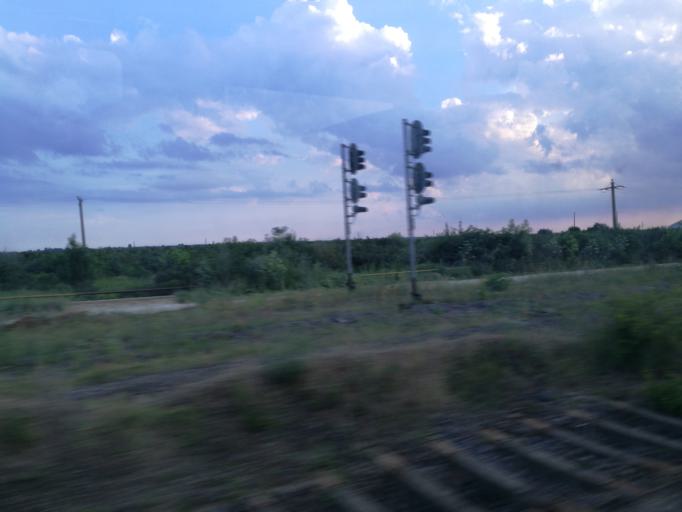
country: RO
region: Dambovita
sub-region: Comuna Produlesti
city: Costestii din Deal
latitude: 44.6732
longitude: 25.5054
